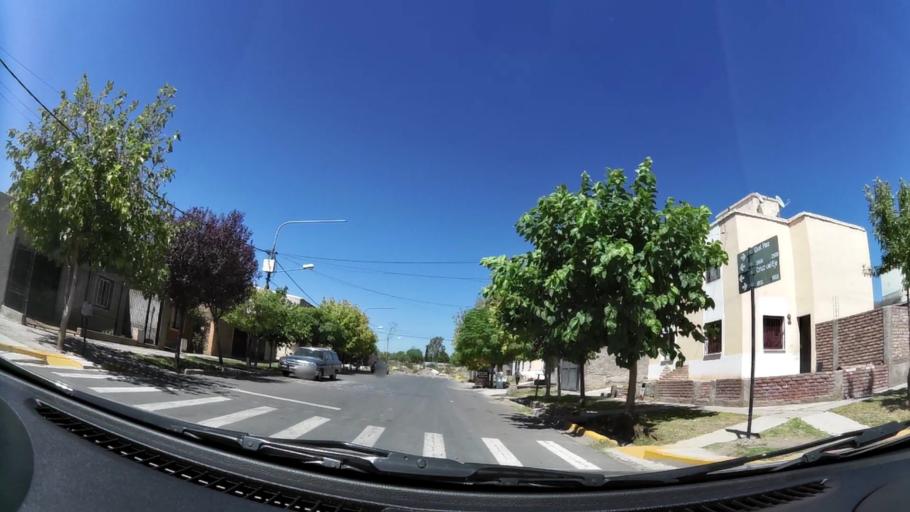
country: AR
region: Mendoza
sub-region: Departamento de Godoy Cruz
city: Godoy Cruz
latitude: -32.9407
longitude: -68.8740
